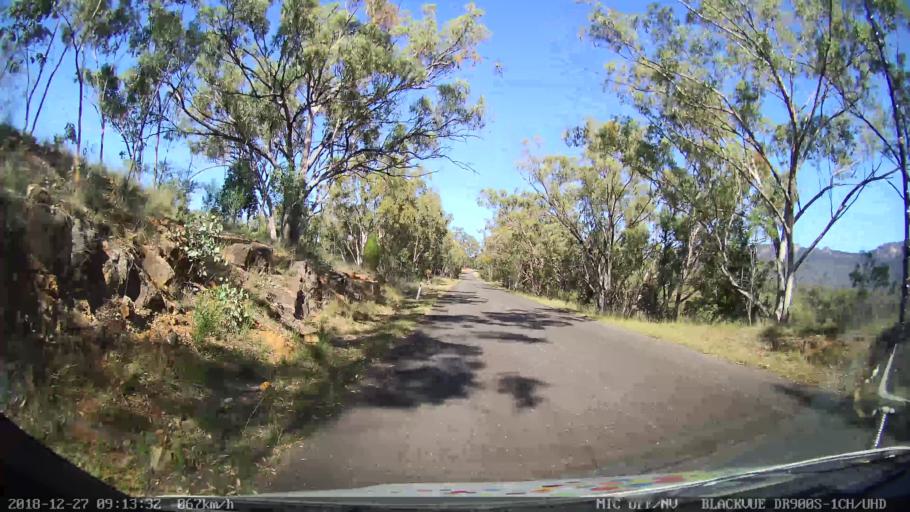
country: AU
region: New South Wales
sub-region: Lithgow
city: Portland
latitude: -33.1377
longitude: 150.0927
